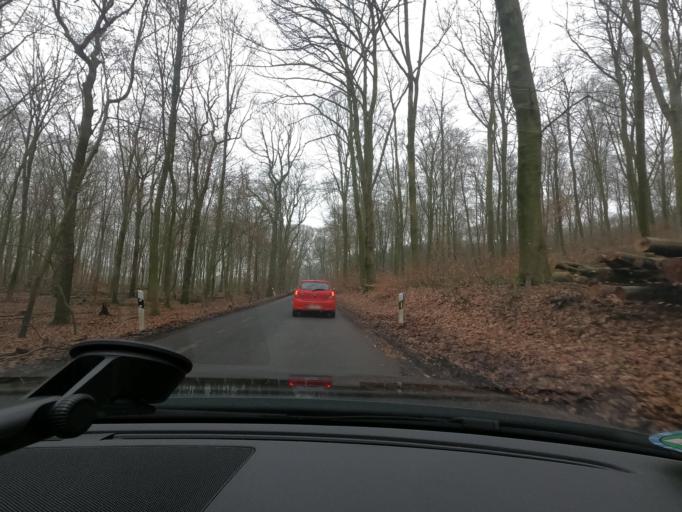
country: DE
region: North Rhine-Westphalia
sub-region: Regierungsbezirk Dusseldorf
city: Krefeld
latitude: 51.3881
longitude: 6.5442
